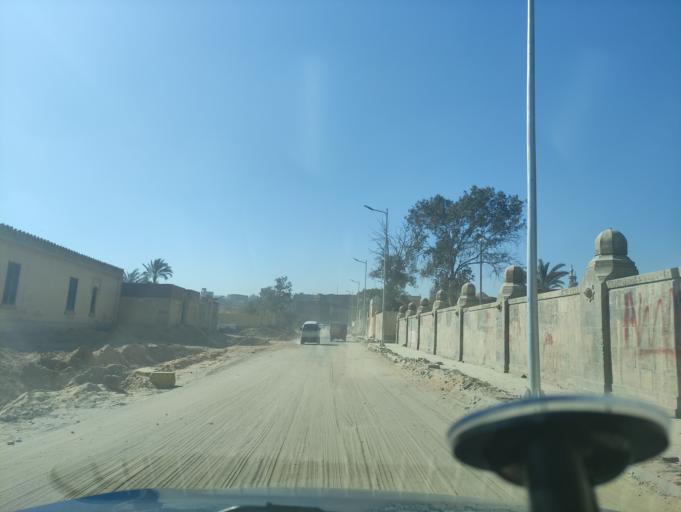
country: EG
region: Muhafazat al Qahirah
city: Cairo
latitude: 30.0520
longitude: 31.2802
